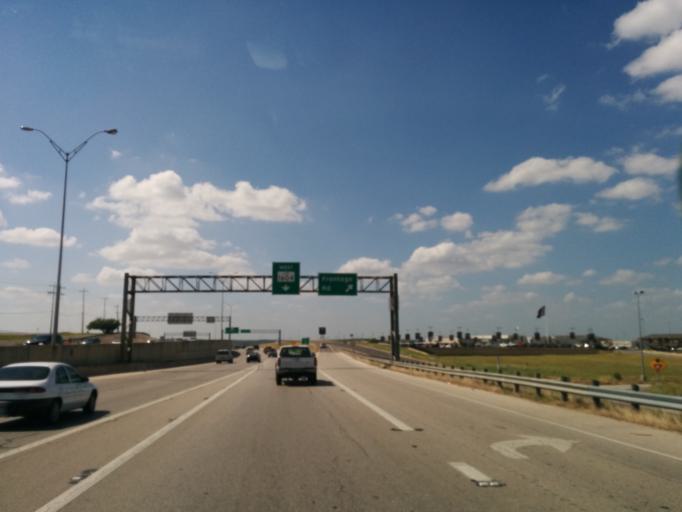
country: US
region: Texas
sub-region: Bexar County
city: Live Oak
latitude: 29.5718
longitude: -98.3364
